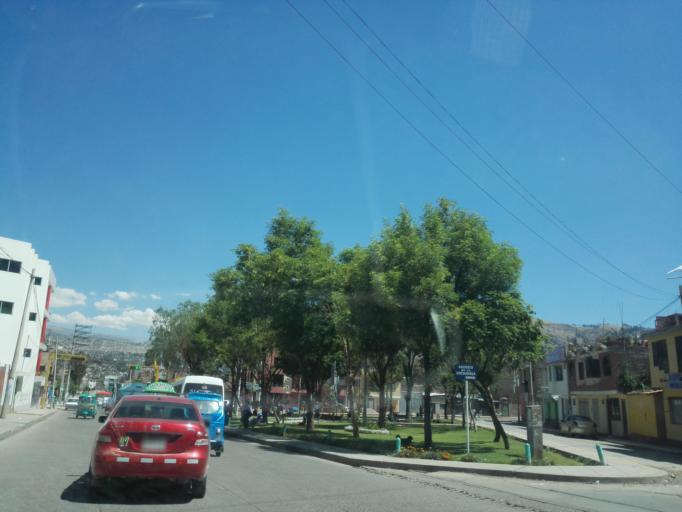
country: PE
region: Ayacucho
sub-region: Provincia de Huamanga
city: Ayacucho
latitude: -13.1497
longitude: -74.2279
